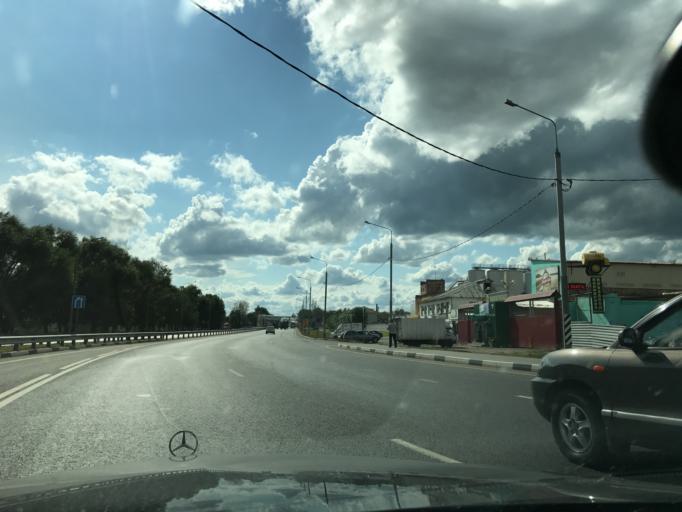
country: RU
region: Vladimir
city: Lakinsk
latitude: 56.0194
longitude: 39.9707
